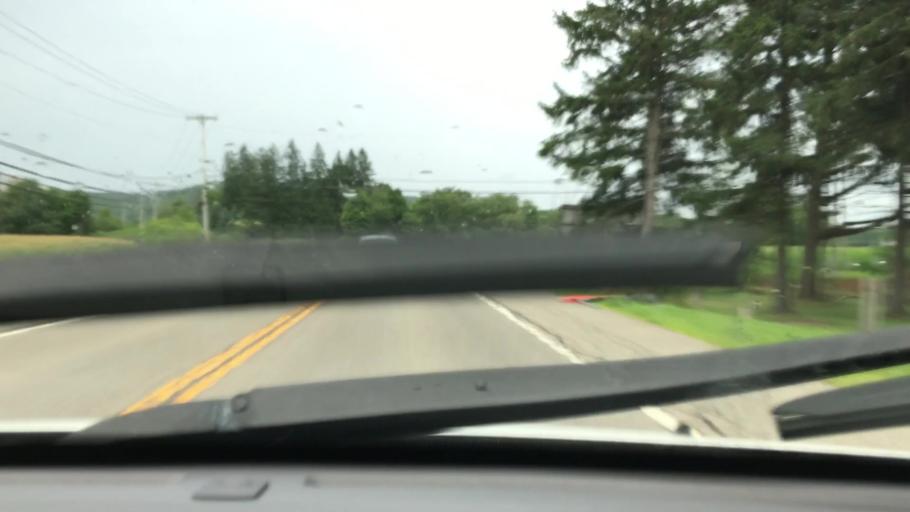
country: US
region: New York
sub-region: Cattaraugus County
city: Salamanca
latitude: 42.1966
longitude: -78.6530
